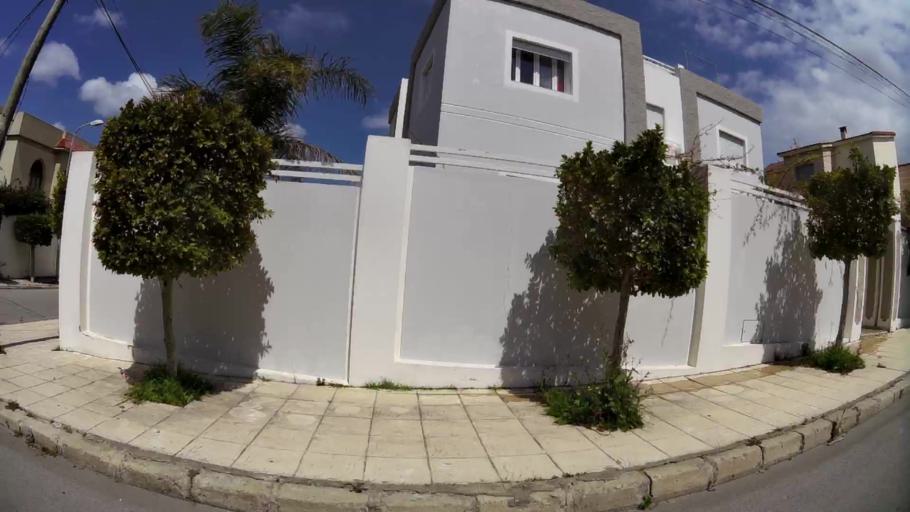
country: MA
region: Tanger-Tetouan
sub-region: Tanger-Assilah
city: Tangier
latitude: 35.7728
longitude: -5.7669
